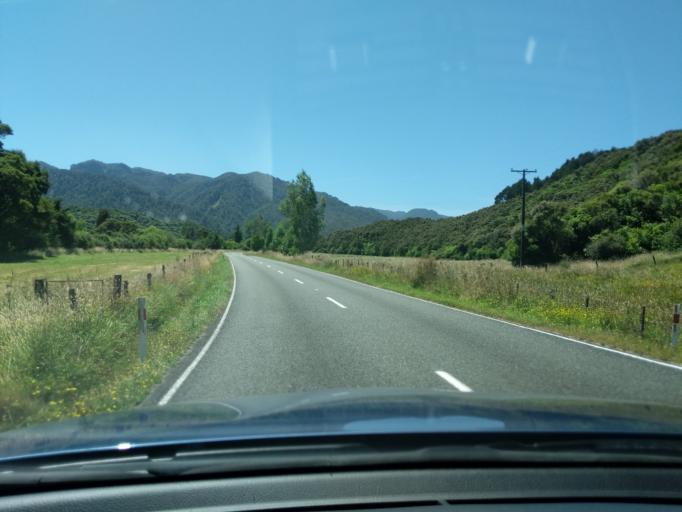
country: NZ
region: Tasman
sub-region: Tasman District
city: Takaka
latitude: -40.7337
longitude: 172.5822
